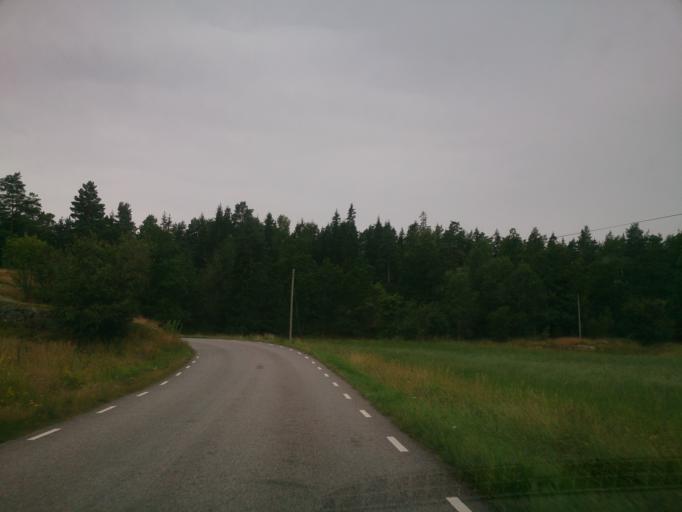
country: SE
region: OEstergoetland
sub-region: Valdemarsviks Kommun
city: Valdemarsvik
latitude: 58.2727
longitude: 16.7381
